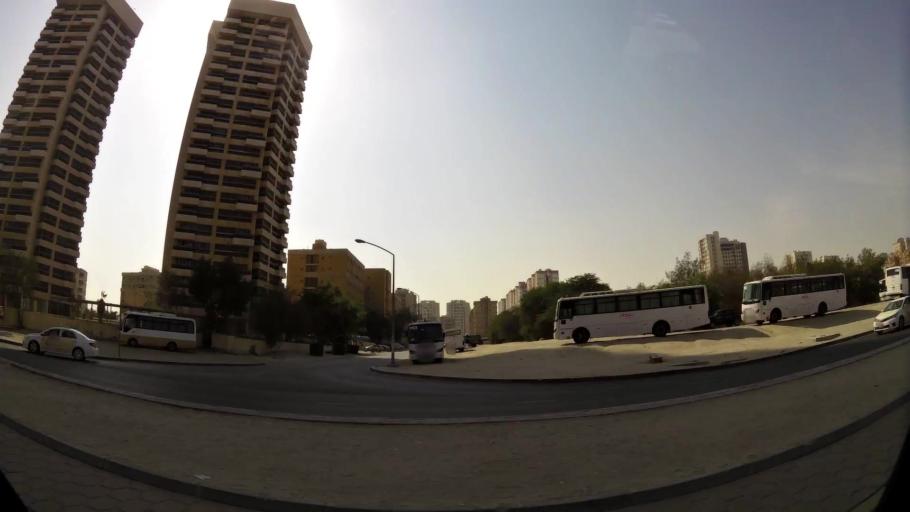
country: KW
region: Al Ahmadi
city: Al Mahbulah
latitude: 29.1410
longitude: 48.1210
